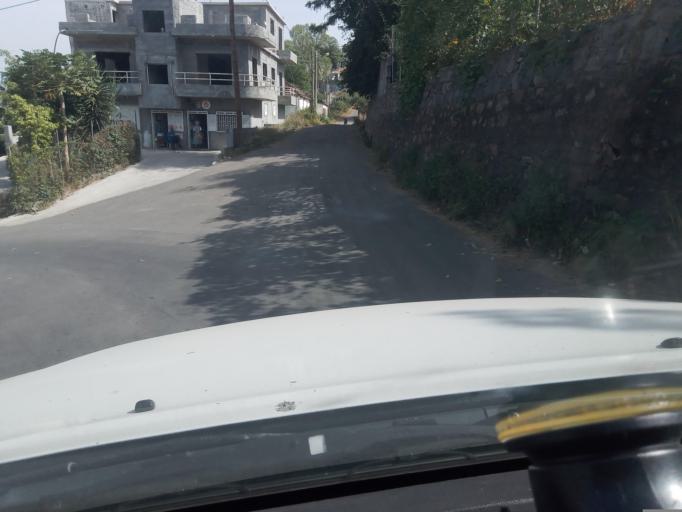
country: CV
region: Santa Catarina
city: Assomada
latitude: 15.1326
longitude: -23.6659
